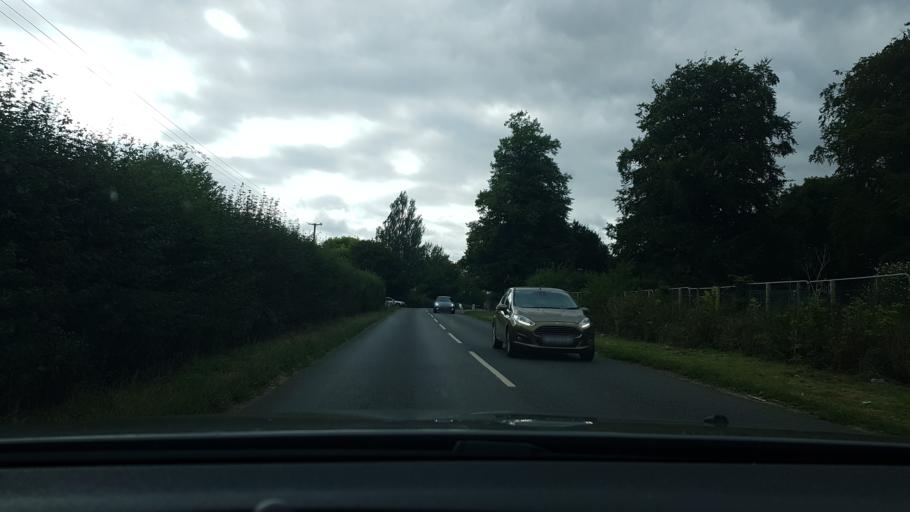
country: GB
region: England
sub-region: West Berkshire
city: Hermitage
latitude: 51.4583
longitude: -1.3014
